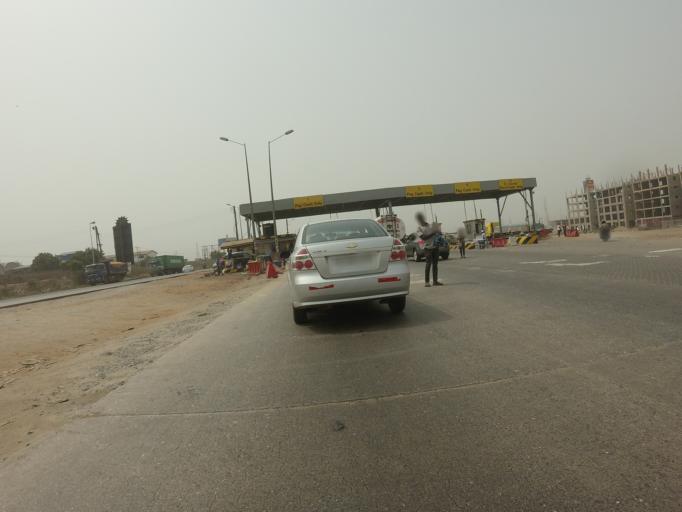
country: GH
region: Greater Accra
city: Tema
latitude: 5.6838
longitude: -0.0224
